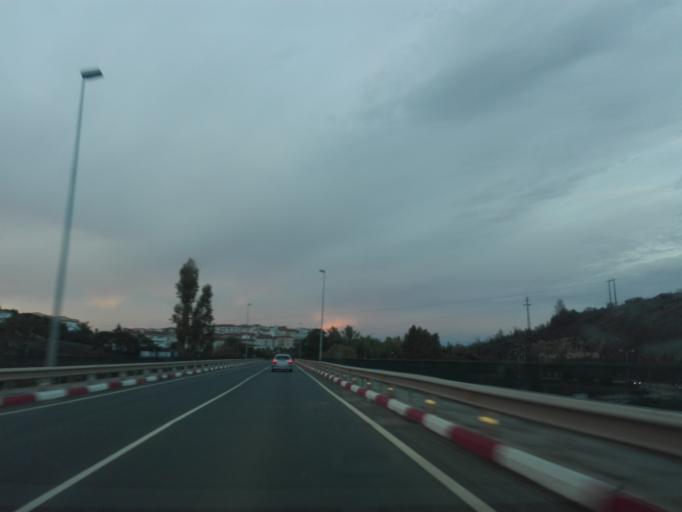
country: ES
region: Extremadura
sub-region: Provincia de Caceres
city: Coria
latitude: 39.9788
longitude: -6.5281
